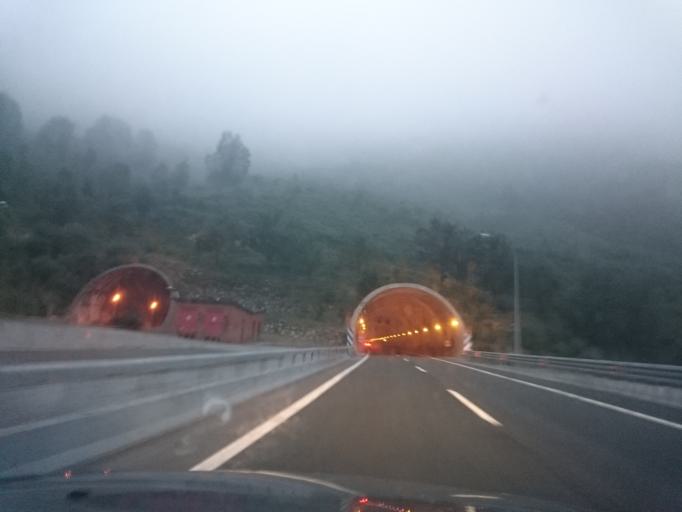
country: ES
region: Castille and Leon
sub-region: Provincia de Leon
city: Sena de Luna
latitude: 42.9942
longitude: -5.8158
